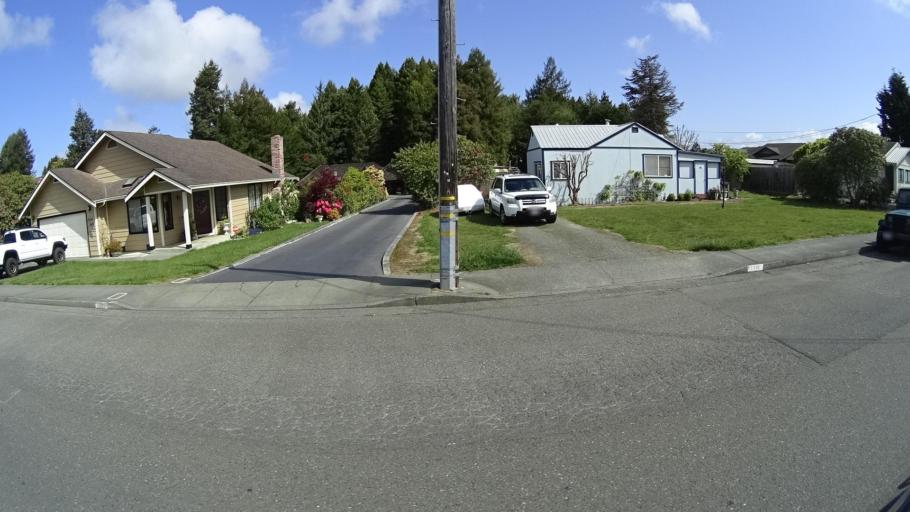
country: US
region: California
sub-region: Humboldt County
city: Cutten
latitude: 40.7586
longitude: -124.1515
